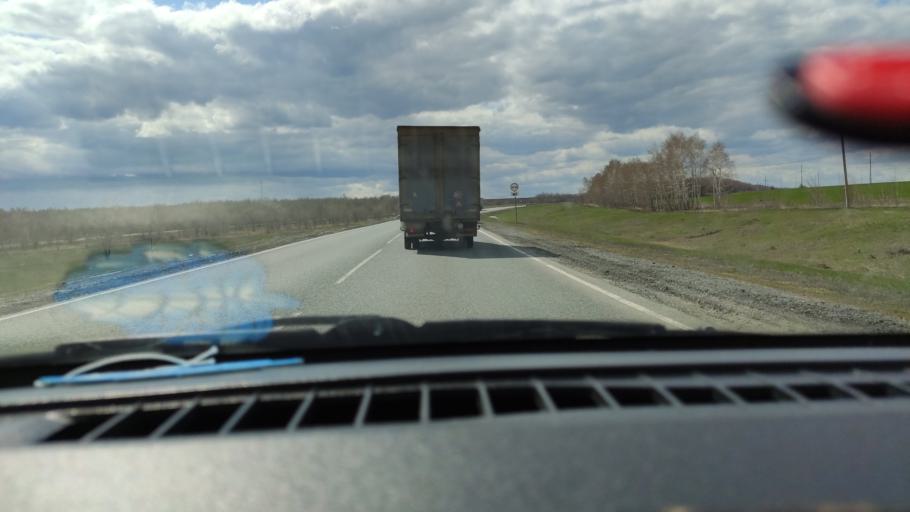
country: RU
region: Saratov
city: Balakovo
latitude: 52.1092
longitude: 47.7467
